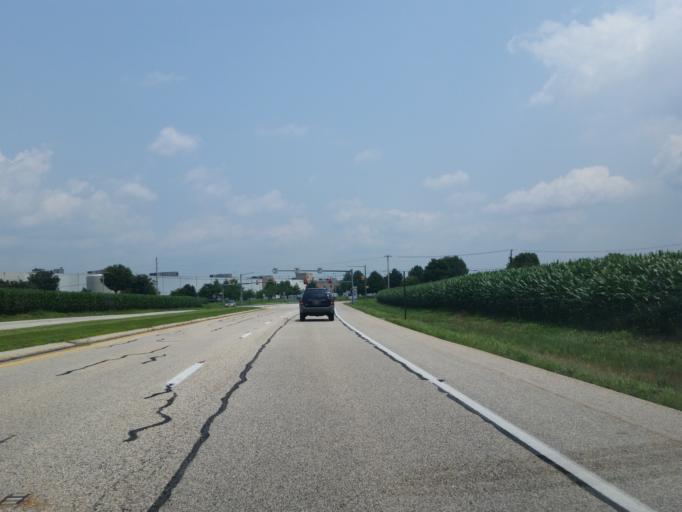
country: US
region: Pennsylvania
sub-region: Dauphin County
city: Palmdale
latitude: 40.3073
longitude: -76.6195
